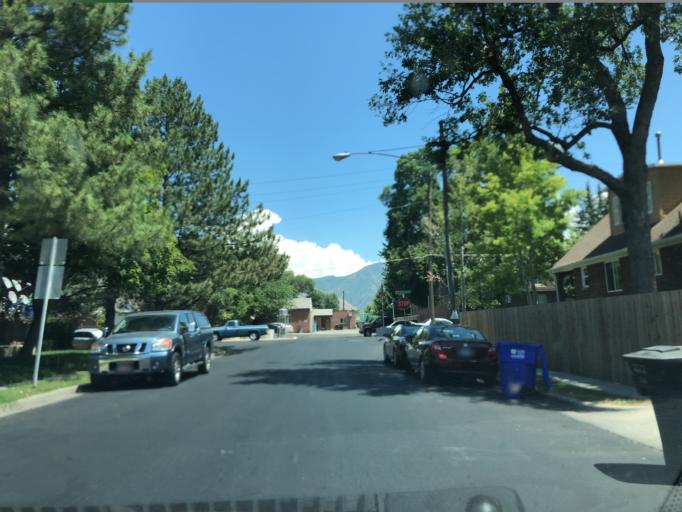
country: US
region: Utah
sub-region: Salt Lake County
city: South Salt Lake
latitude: 40.7163
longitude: -111.8833
